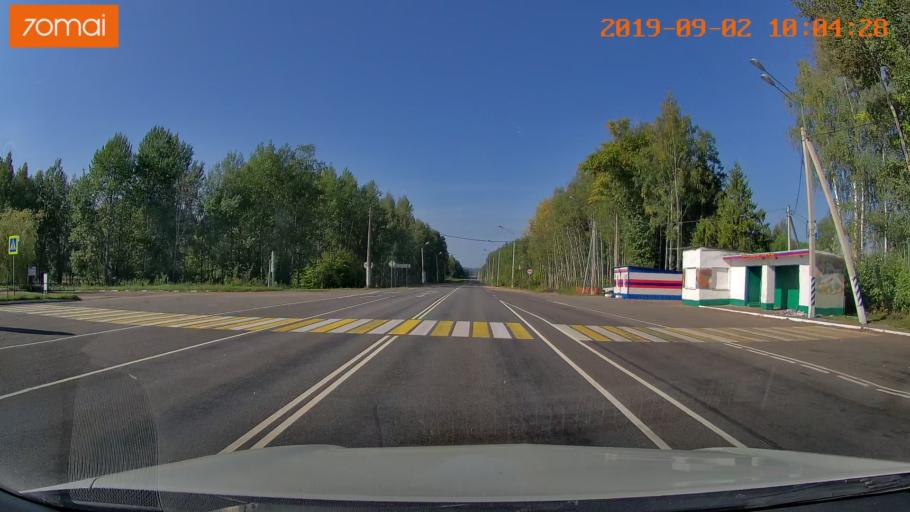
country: RU
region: Kaluga
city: Baryatino
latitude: 54.4932
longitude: 34.4450
